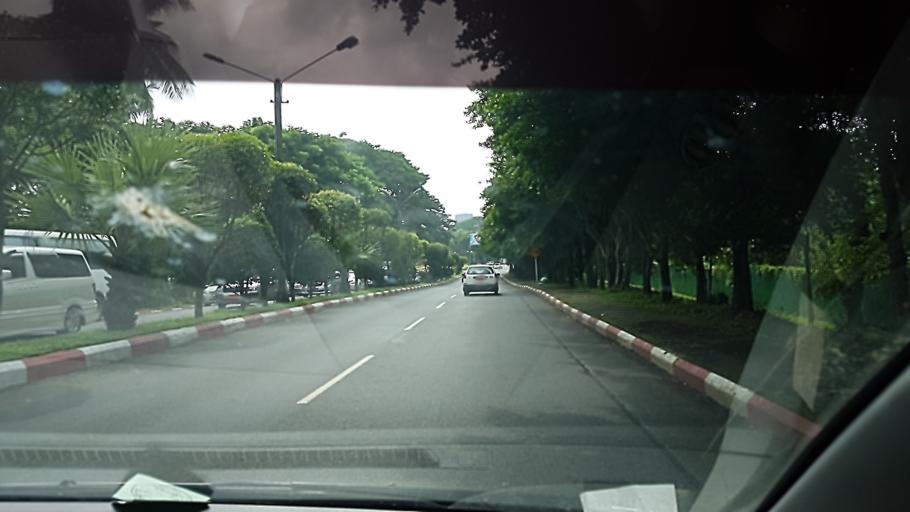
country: MM
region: Yangon
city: Yangon
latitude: 16.7961
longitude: 96.1544
